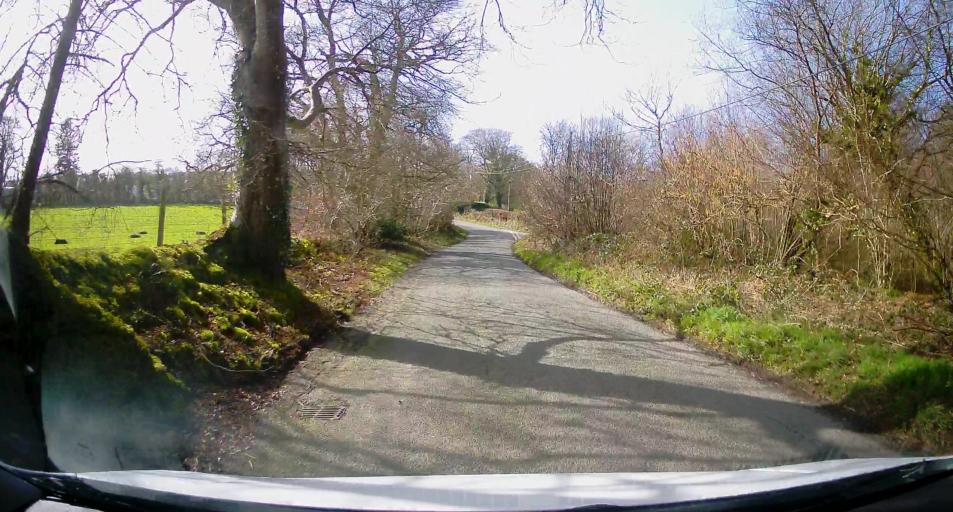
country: GB
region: Wales
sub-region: County of Ceredigion
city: Aberporth
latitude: 52.0825
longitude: -4.5431
